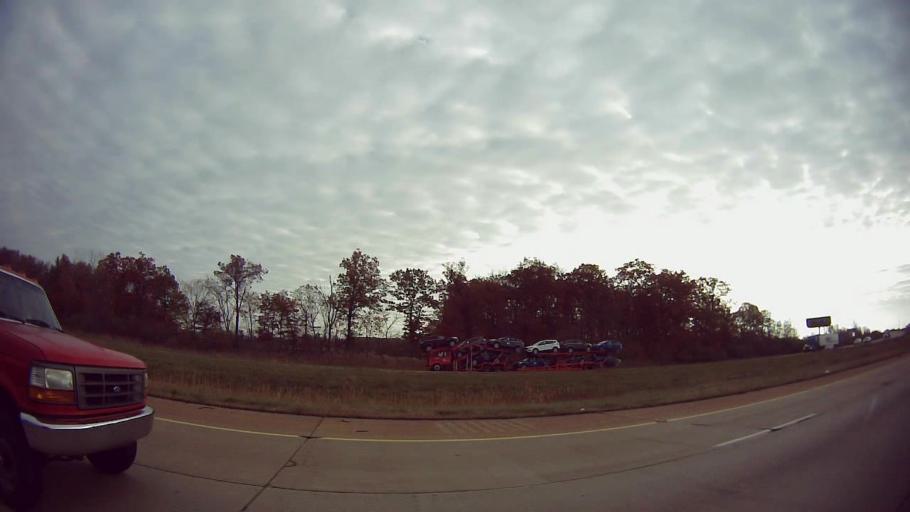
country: US
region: Michigan
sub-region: Monroe County
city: Carleton
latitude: 42.0863
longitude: -83.3774
